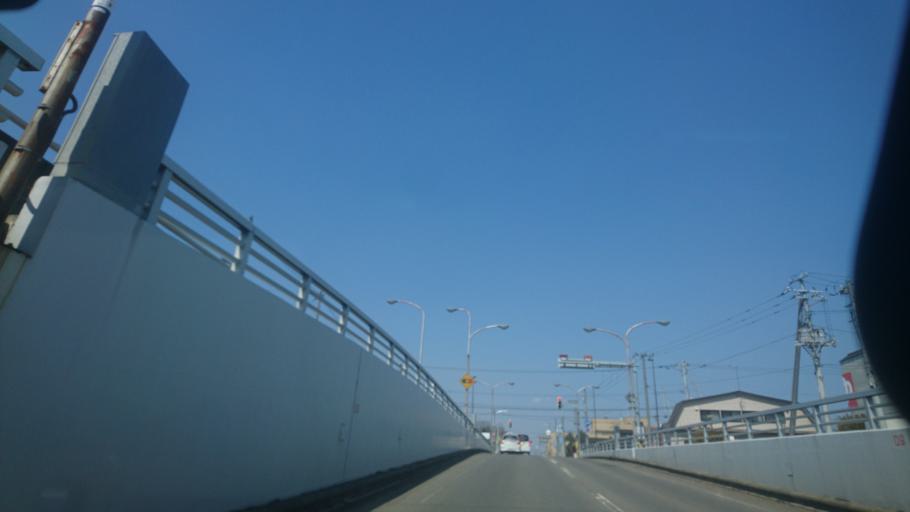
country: JP
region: Hokkaido
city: Obihiro
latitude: 42.9105
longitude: 143.0545
